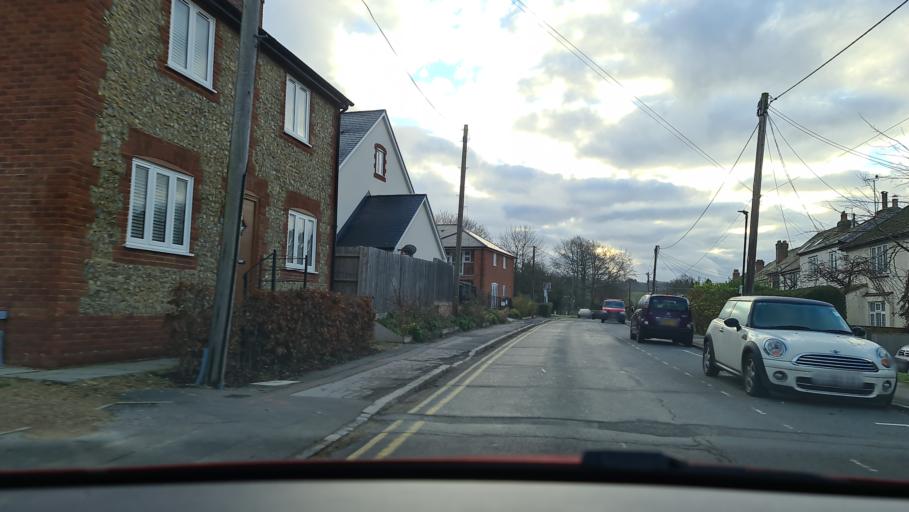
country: GB
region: England
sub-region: Buckinghamshire
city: Princes Risborough
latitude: 51.7177
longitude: -0.8379
